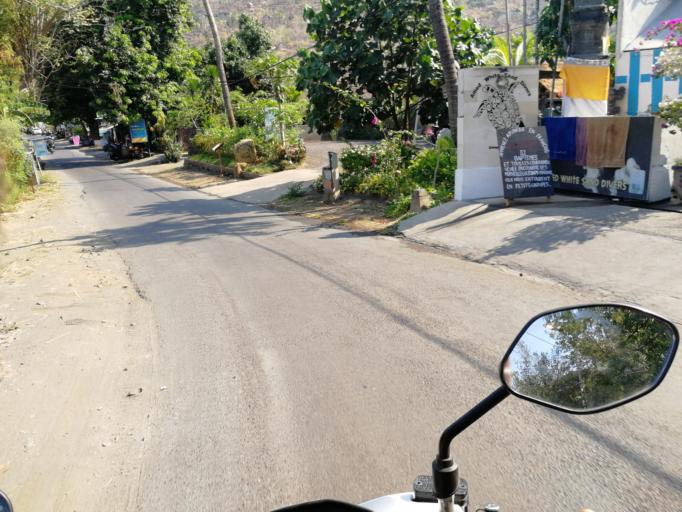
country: ID
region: Bali
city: Biaslantang Kaler
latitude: -8.3481
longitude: 115.6804
